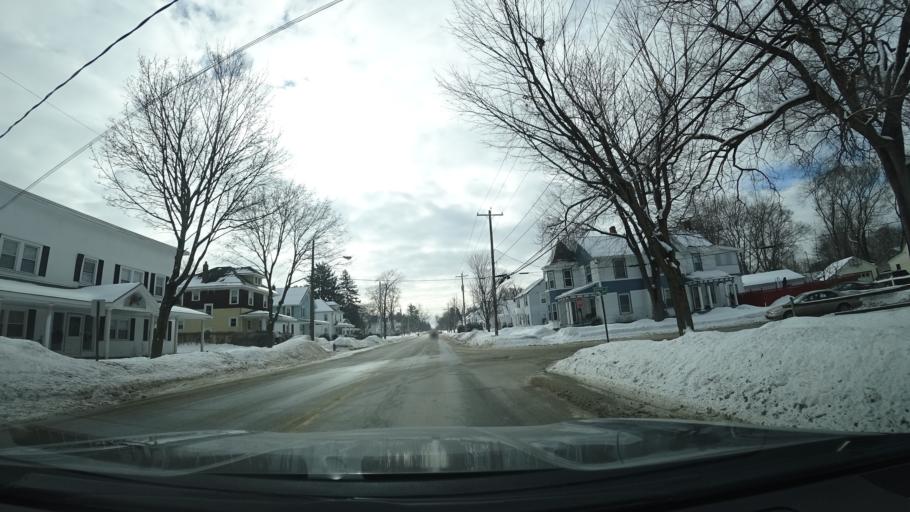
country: US
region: New York
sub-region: Saratoga County
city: South Glens Falls
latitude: 43.2955
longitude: -73.6319
